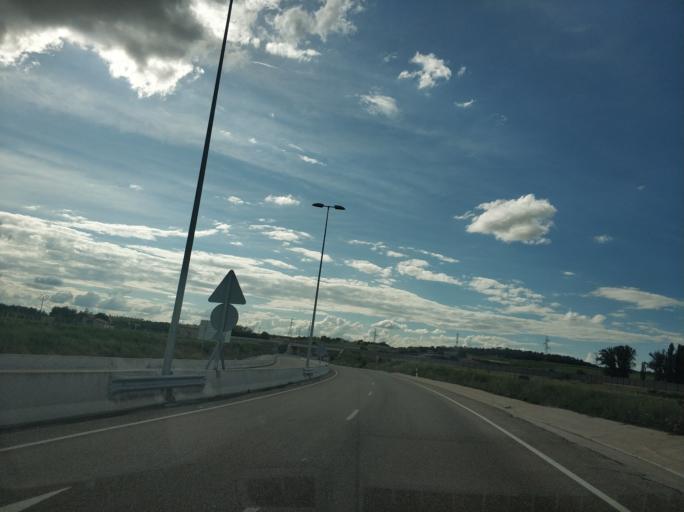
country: ES
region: Castille and Leon
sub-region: Provincia de Burgos
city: Aranda de Duero
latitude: 41.6922
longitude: -3.6697
